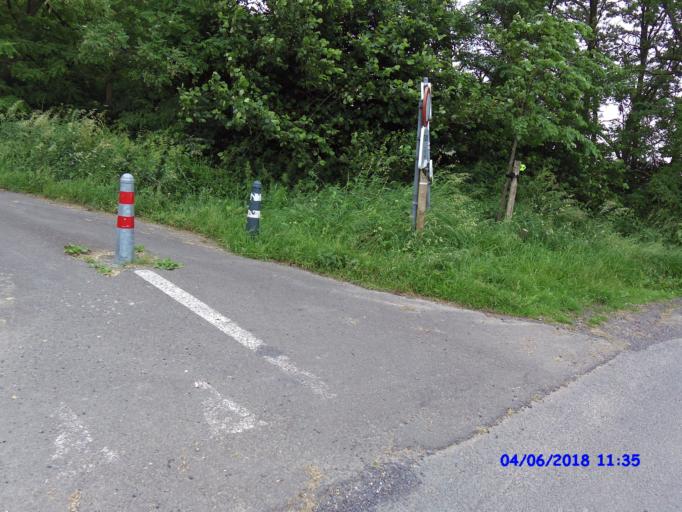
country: BE
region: Flanders
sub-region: Provincie West-Vlaanderen
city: Staden
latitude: 50.9647
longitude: 2.9962
